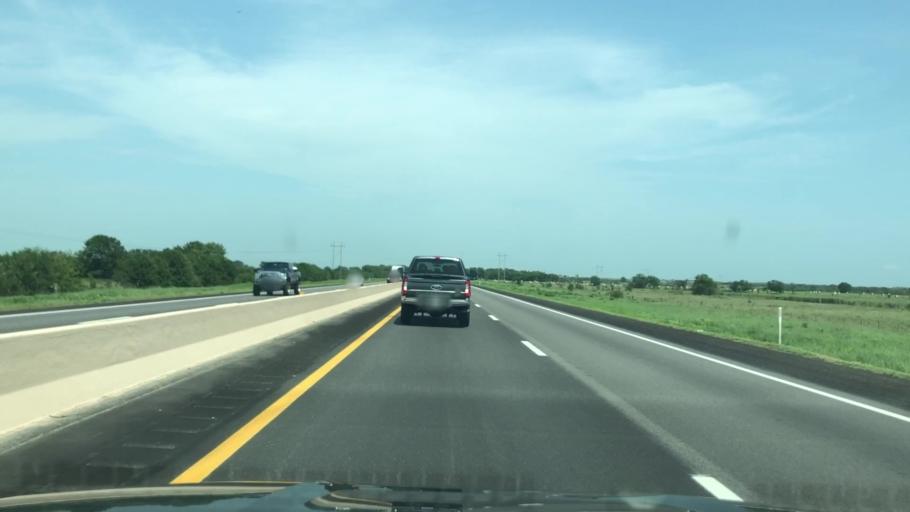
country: US
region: Oklahoma
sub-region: Craig County
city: Vinita
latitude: 36.6717
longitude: -95.0643
